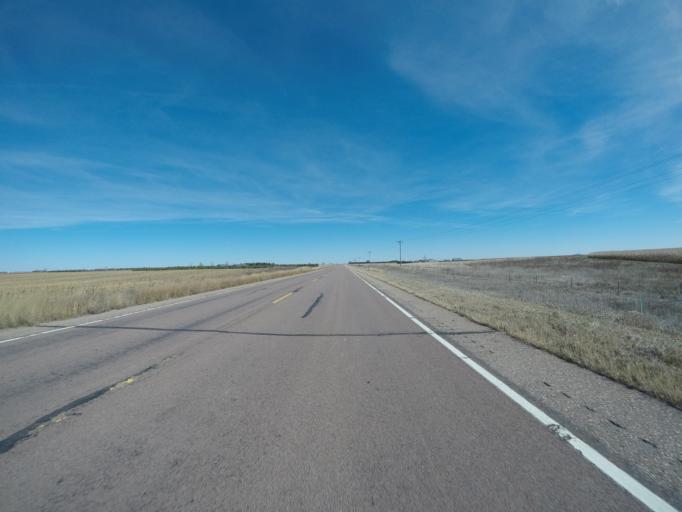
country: US
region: Colorado
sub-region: Yuma County
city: Yuma
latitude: 39.6560
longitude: -102.6433
